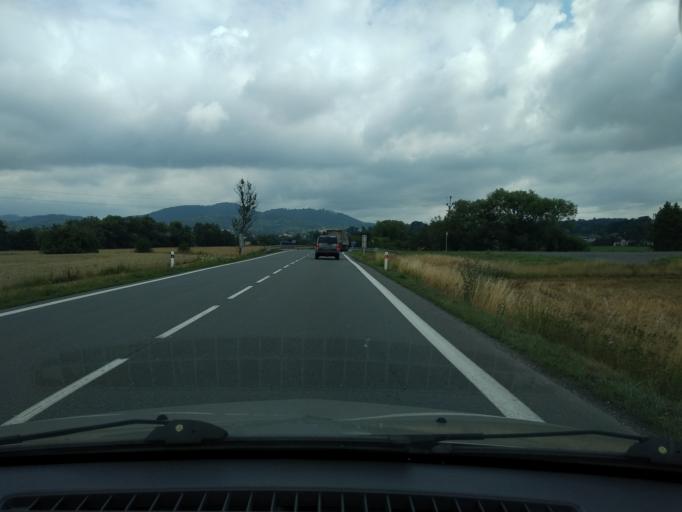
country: CZ
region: Olomoucky
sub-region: Okres Sumperk
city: Bludov
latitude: 49.9298
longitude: 16.9226
